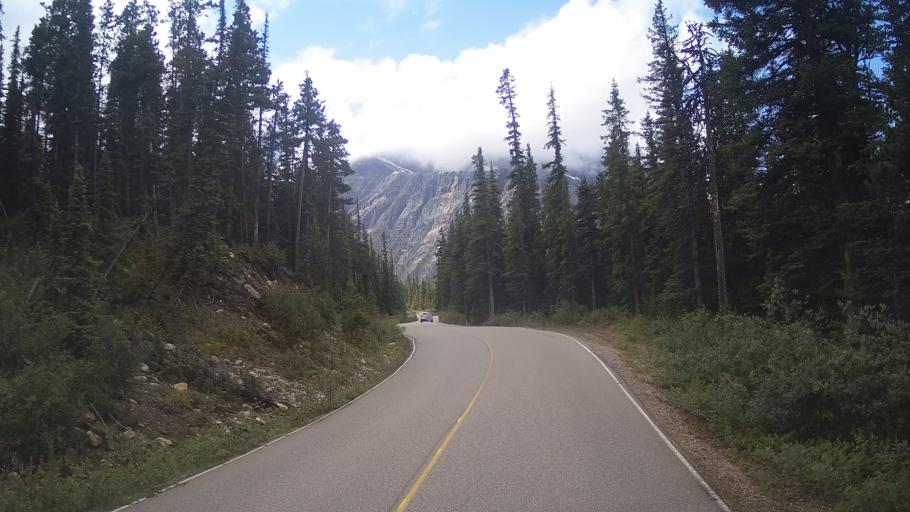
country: CA
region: Alberta
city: Jasper Park Lodge
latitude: 52.7134
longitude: -118.0550
